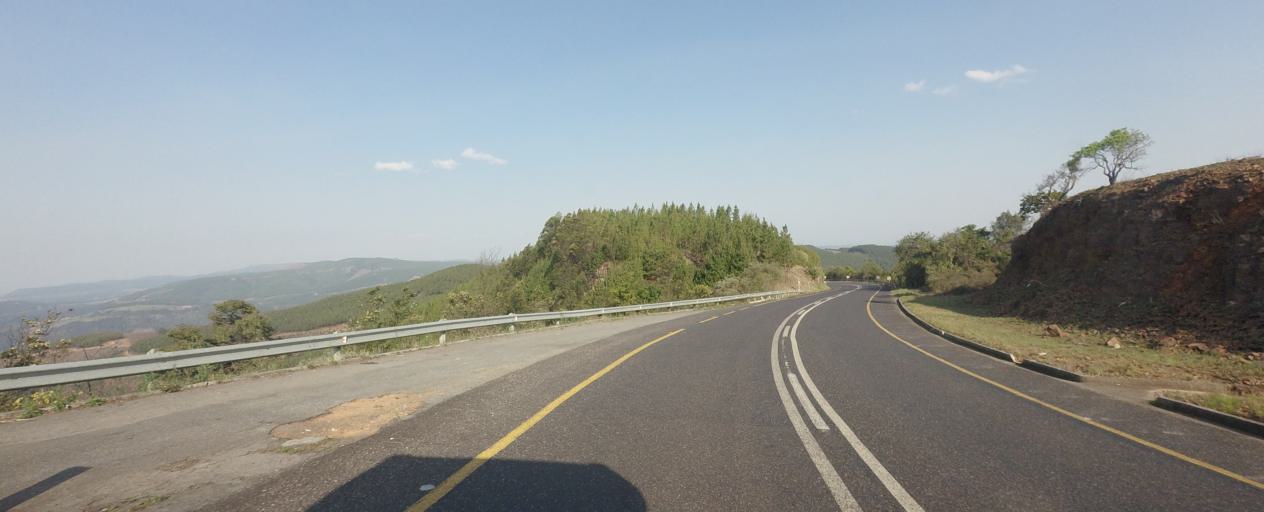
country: ZA
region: Mpumalanga
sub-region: Ehlanzeni District
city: Lydenburg
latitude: -25.1636
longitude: 30.6810
